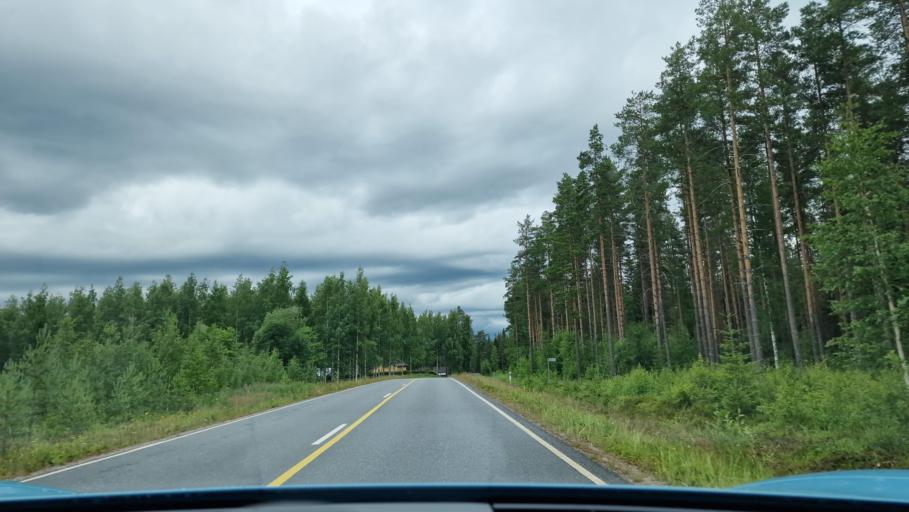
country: FI
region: Southern Ostrobothnia
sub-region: Jaerviseutu
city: Soini
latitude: 62.6919
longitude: 24.4610
